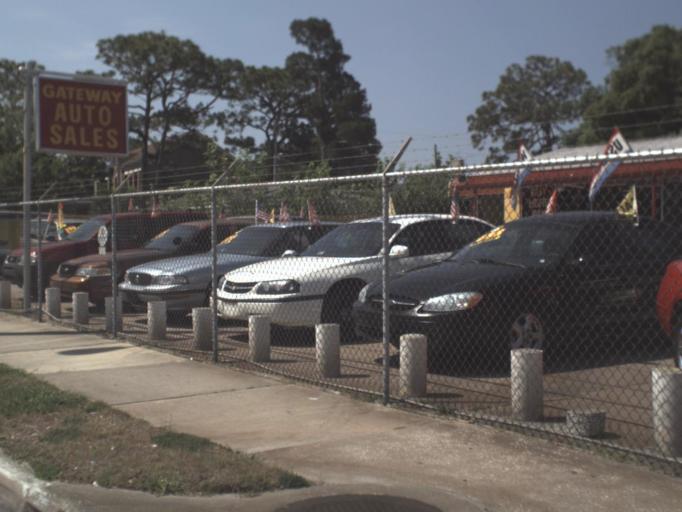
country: US
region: Florida
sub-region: Duval County
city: Jacksonville
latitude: 30.3801
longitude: -81.6703
